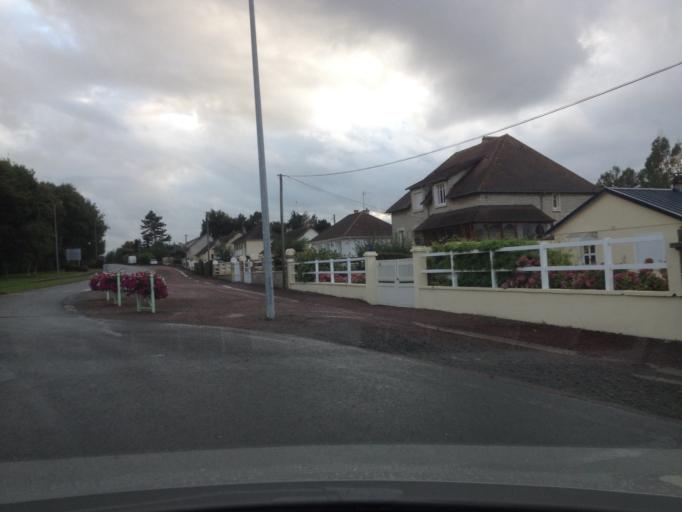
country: FR
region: Lower Normandy
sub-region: Departement du Calvados
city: Grandcamp-Maisy
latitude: 49.3861
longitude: -1.0504
